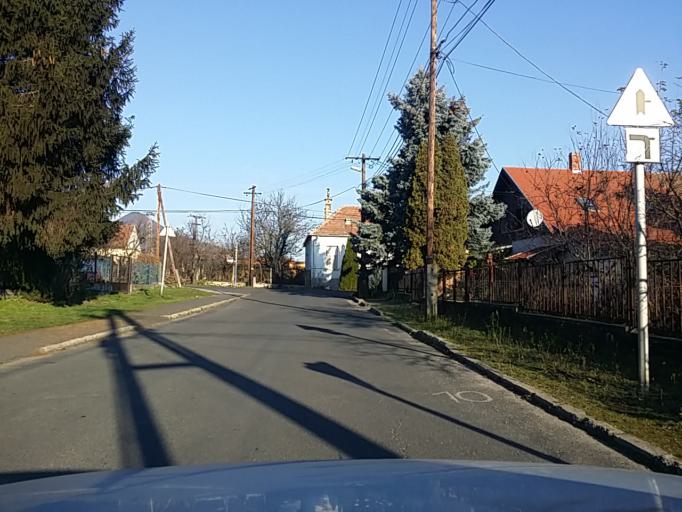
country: HU
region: Veszprem
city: Badacsonytomaj
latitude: 46.8081
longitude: 17.5148
